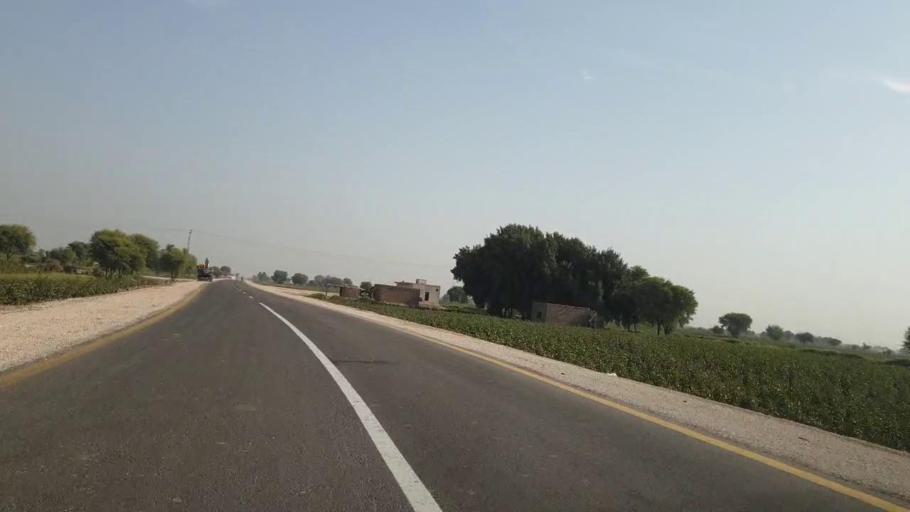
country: PK
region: Sindh
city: Sehwan
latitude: 26.4758
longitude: 67.7869
